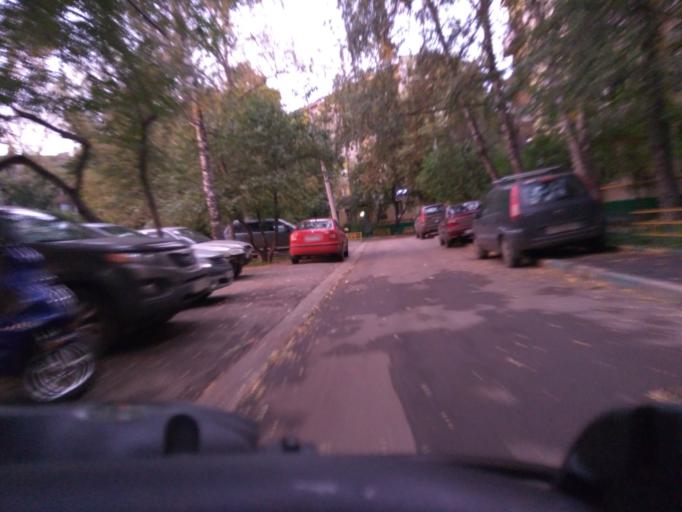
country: RU
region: Moscow
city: Golovinskiy
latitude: 55.8544
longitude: 37.5058
